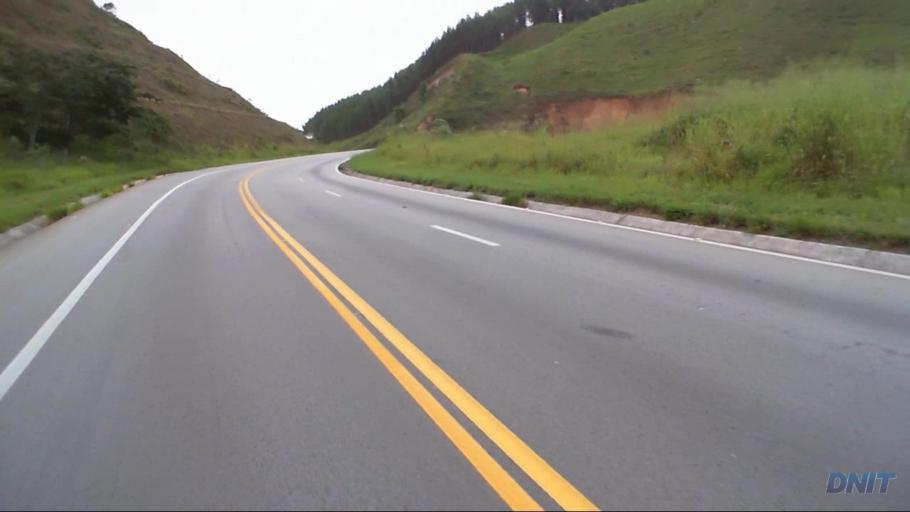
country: BR
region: Minas Gerais
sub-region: Nova Era
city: Nova Era
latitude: -19.6722
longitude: -42.9725
